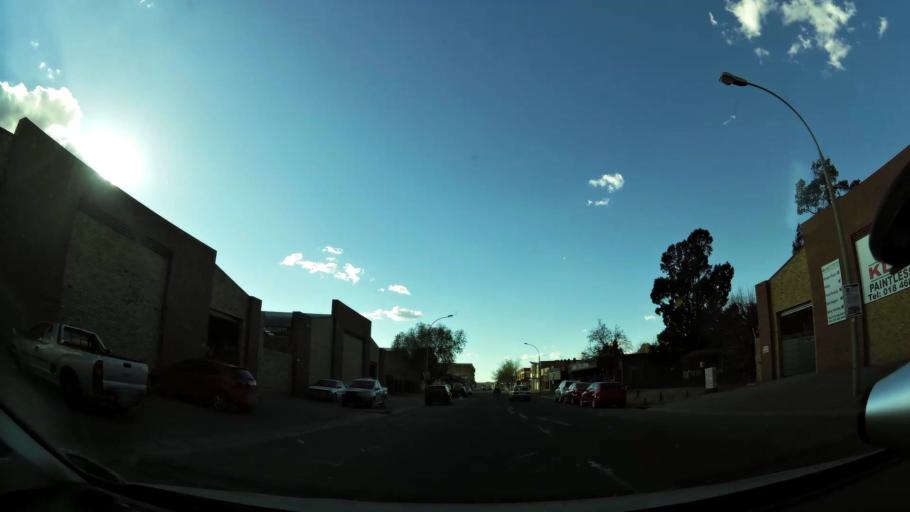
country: ZA
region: North-West
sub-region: Dr Kenneth Kaunda District Municipality
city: Klerksdorp
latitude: -26.8722
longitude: 26.6674
